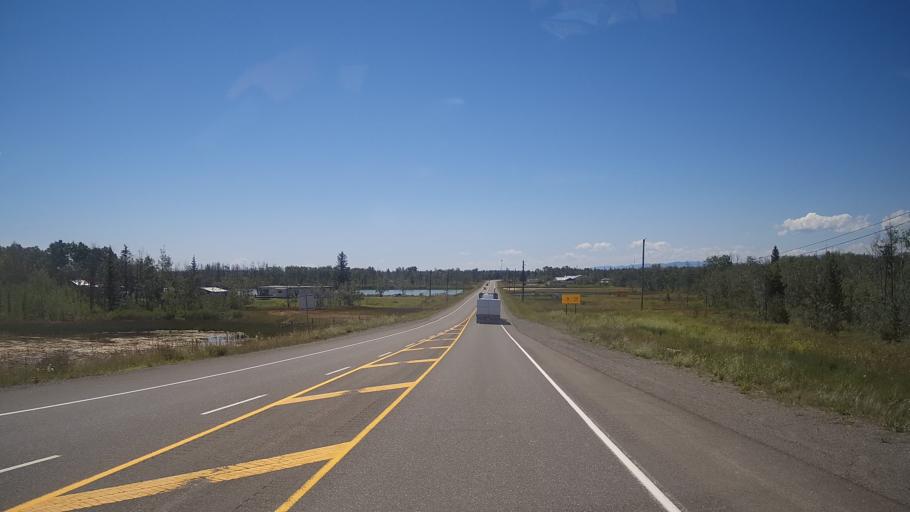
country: CA
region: British Columbia
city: Cache Creek
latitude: 51.3237
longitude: -121.3870
